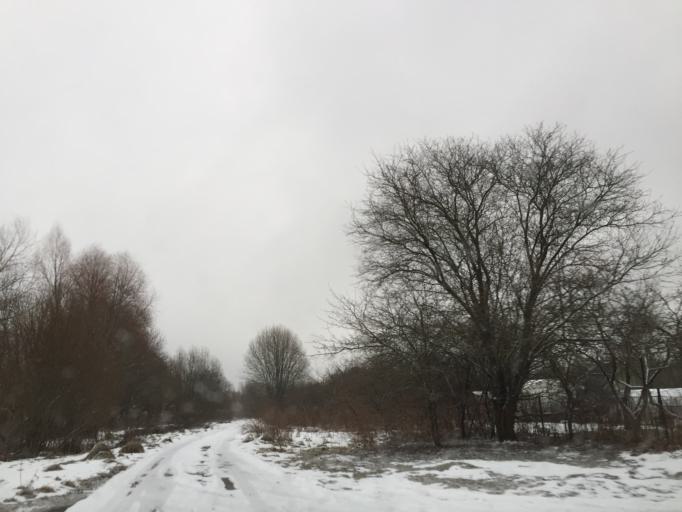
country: LV
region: Riga
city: Riga
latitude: 56.9190
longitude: 24.1371
